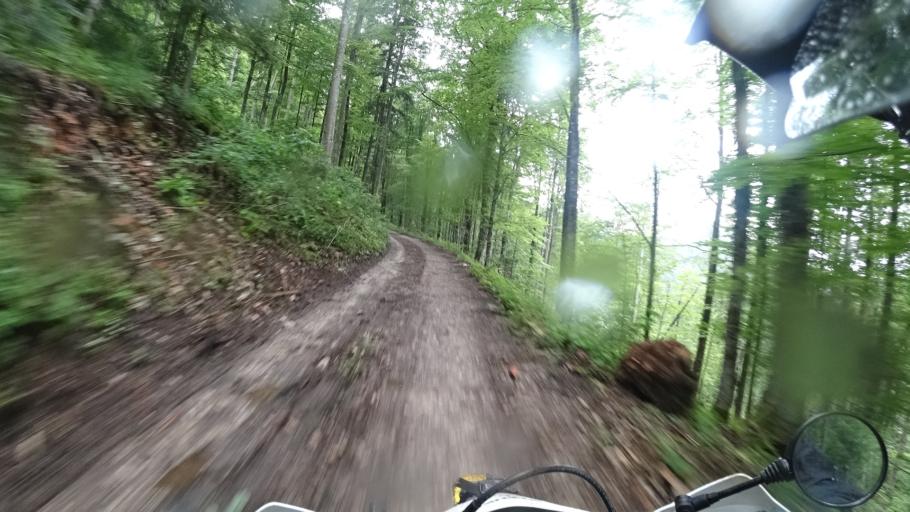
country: HR
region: Primorsko-Goranska
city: Vrbovsko
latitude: 45.2973
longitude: 14.9461
